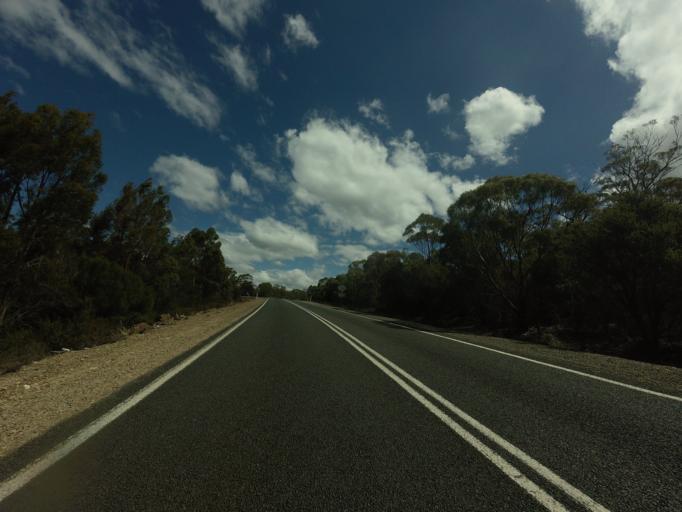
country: AU
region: Tasmania
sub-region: Break O'Day
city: St Helens
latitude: -42.0147
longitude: 147.9592
